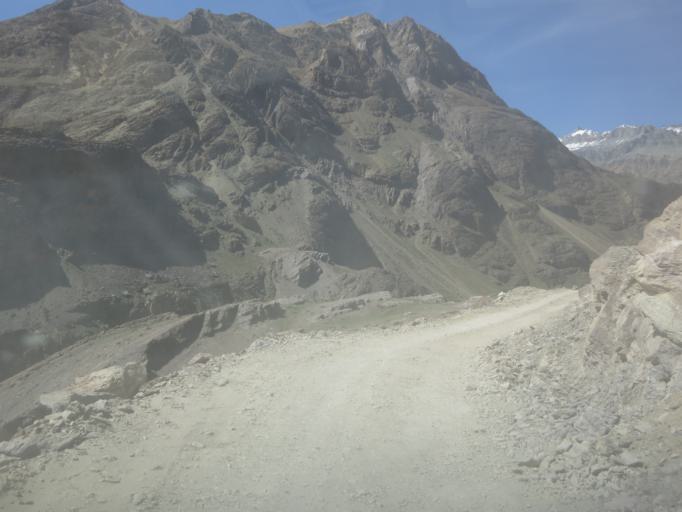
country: IN
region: Himachal Pradesh
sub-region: Kulu
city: Manali
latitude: 32.4327
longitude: 77.6754
